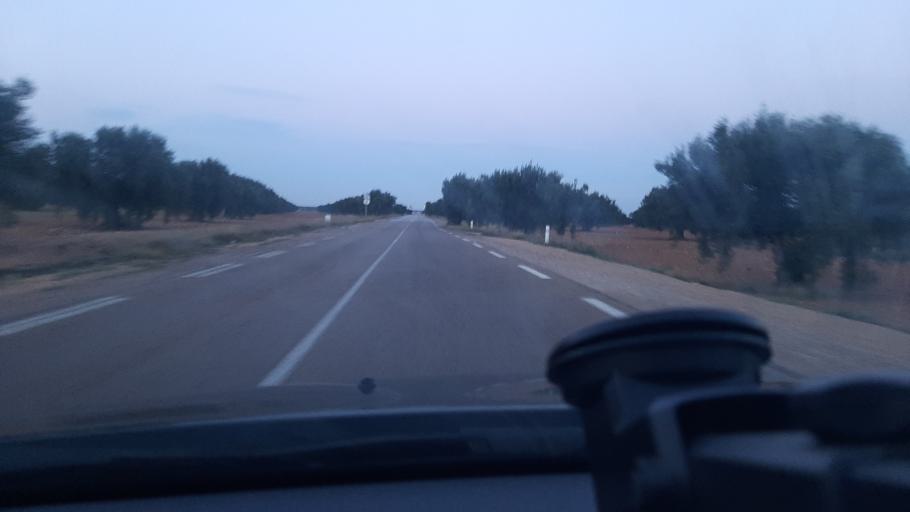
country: TN
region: Al Mahdiyah
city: Shurban
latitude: 35.0354
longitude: 10.5201
